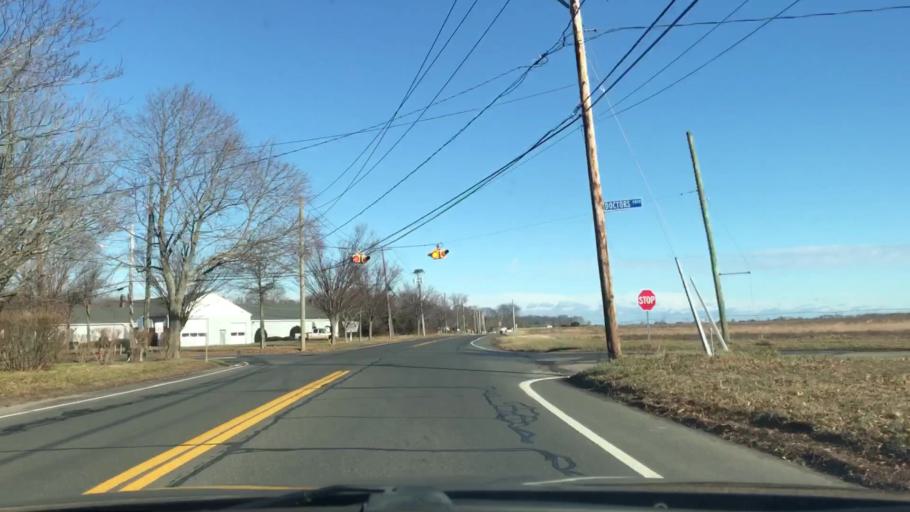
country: US
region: New York
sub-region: Suffolk County
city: Aquebogue
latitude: 40.9457
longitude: -72.6562
